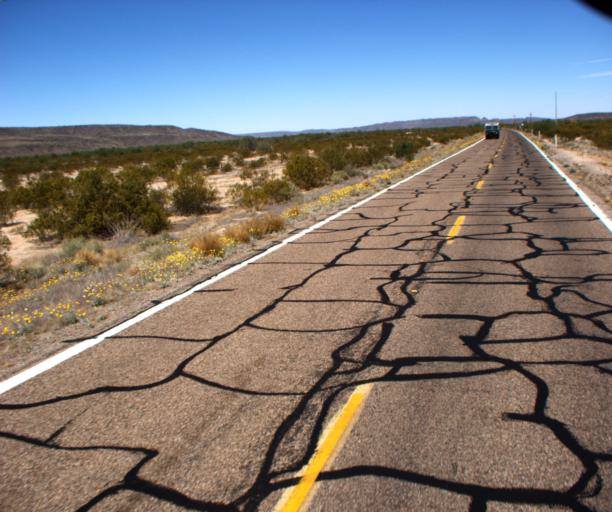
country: US
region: Arizona
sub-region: Pima County
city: Ajo
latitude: 32.4538
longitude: -112.8717
